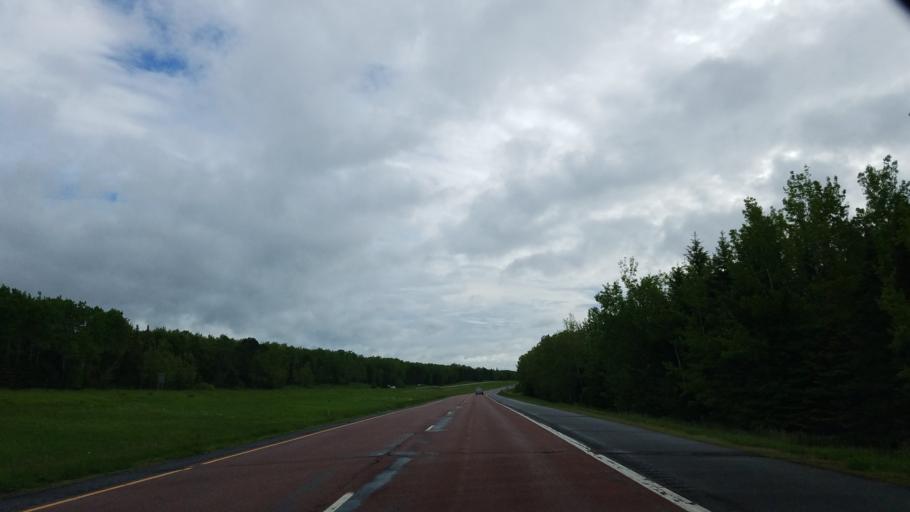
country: US
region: Minnesota
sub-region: Saint Louis County
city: Arnold
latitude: 46.9047
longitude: -91.8945
